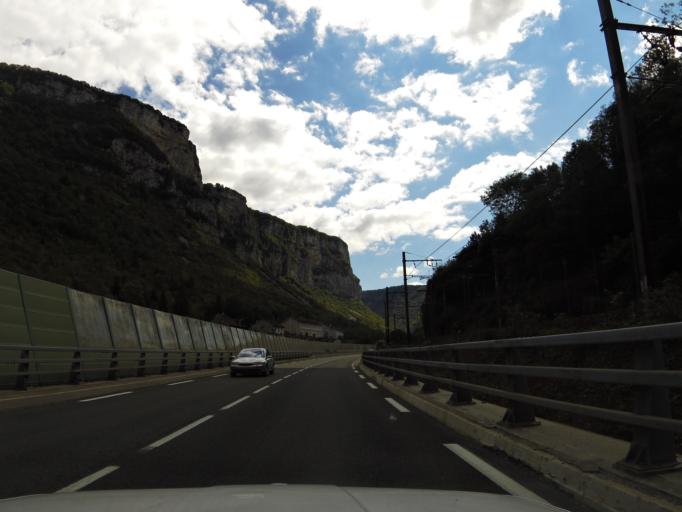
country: FR
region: Rhone-Alpes
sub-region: Departement de l'Ain
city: Tenay
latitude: 45.9180
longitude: 5.5080
